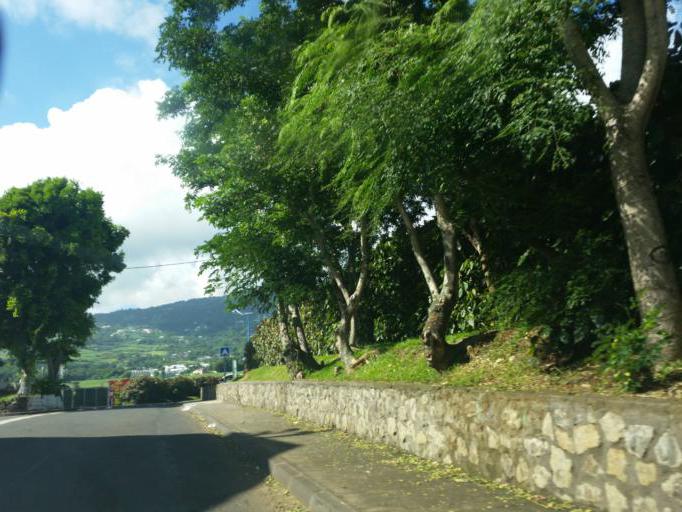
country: RE
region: Reunion
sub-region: Reunion
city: Sainte-Marie
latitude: -20.9219
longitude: 55.5313
